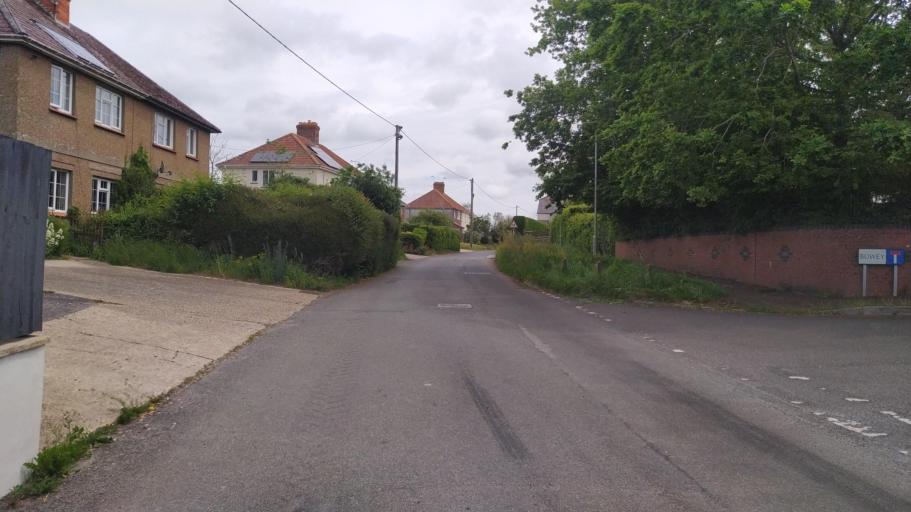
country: GB
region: England
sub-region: Dorset
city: Sturminster Newton
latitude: 50.8990
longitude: -2.2814
